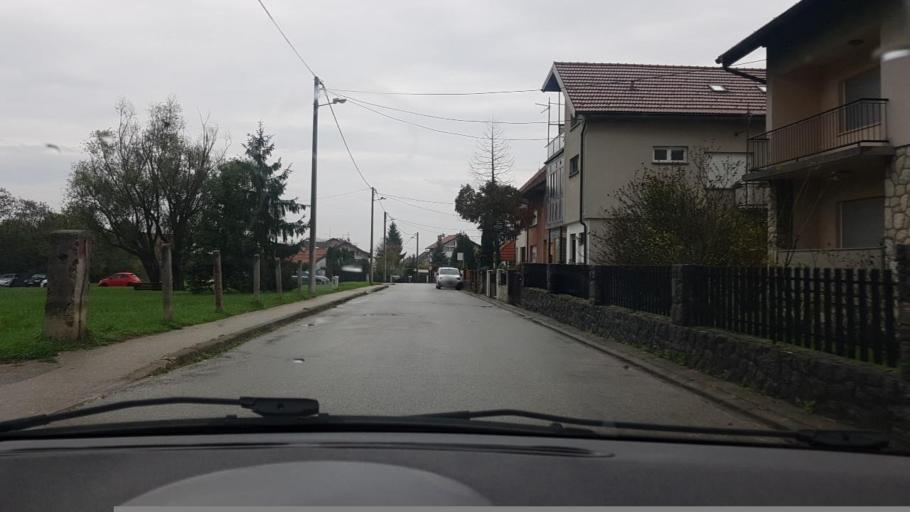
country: HR
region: Grad Zagreb
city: Zagreb
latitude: 45.8307
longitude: 15.9989
